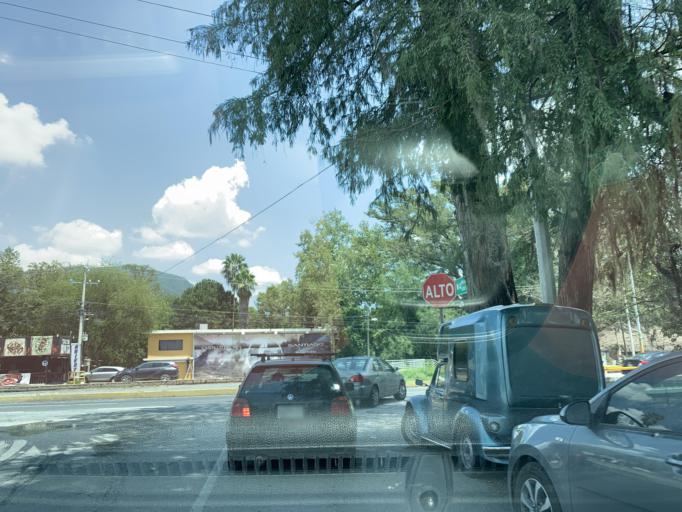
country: MX
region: Nuevo Leon
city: Santiago
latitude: 25.4224
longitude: -100.1468
